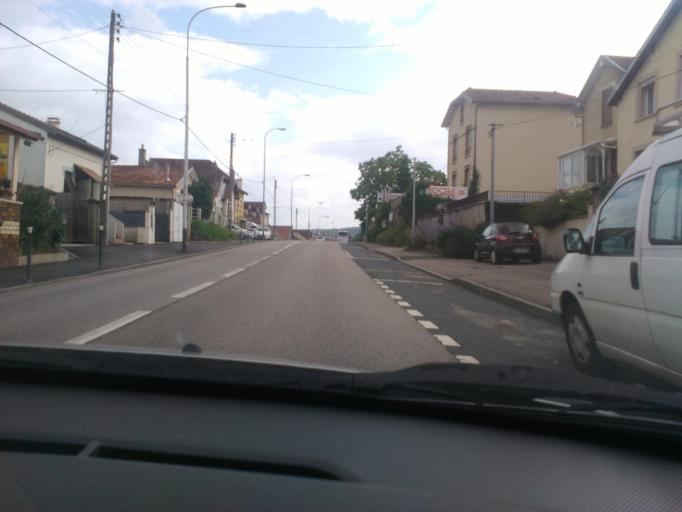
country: FR
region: Lorraine
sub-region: Departement de Meurthe-et-Moselle
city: Pompey
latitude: 48.7779
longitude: 6.1309
